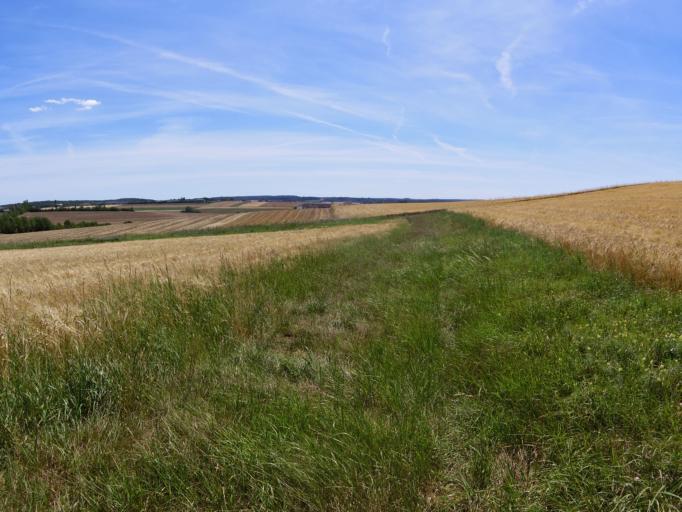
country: DE
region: Bavaria
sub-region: Regierungsbezirk Unterfranken
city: Hettstadt
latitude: 49.8101
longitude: 9.8244
